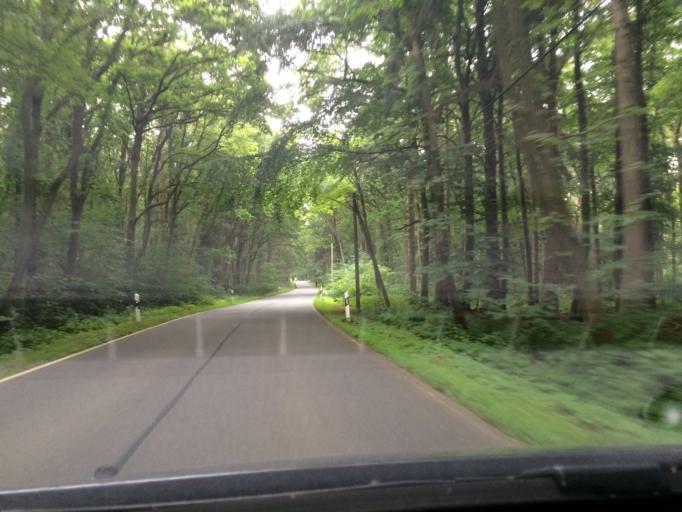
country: DE
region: Mecklenburg-Vorpommern
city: Prohn
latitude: 54.4258
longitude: 13.0239
